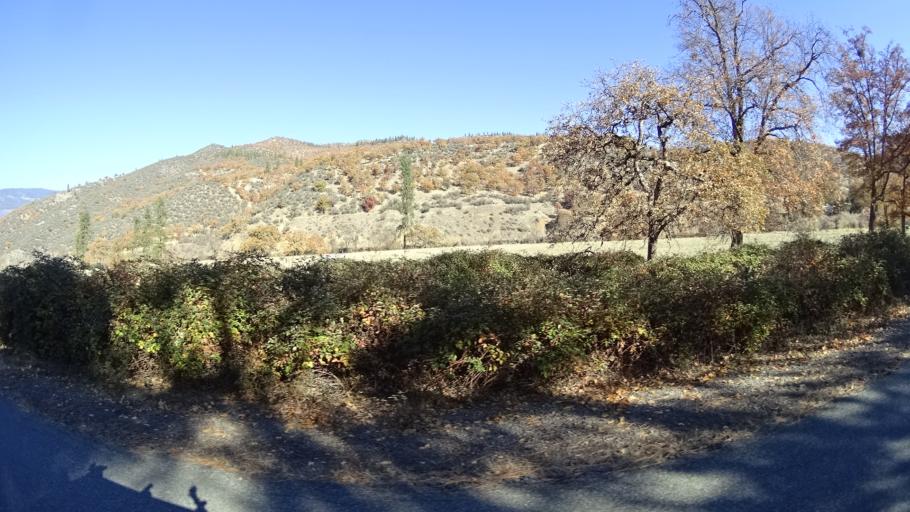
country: US
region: California
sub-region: Siskiyou County
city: Yreka
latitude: 41.8345
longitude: -122.8563
